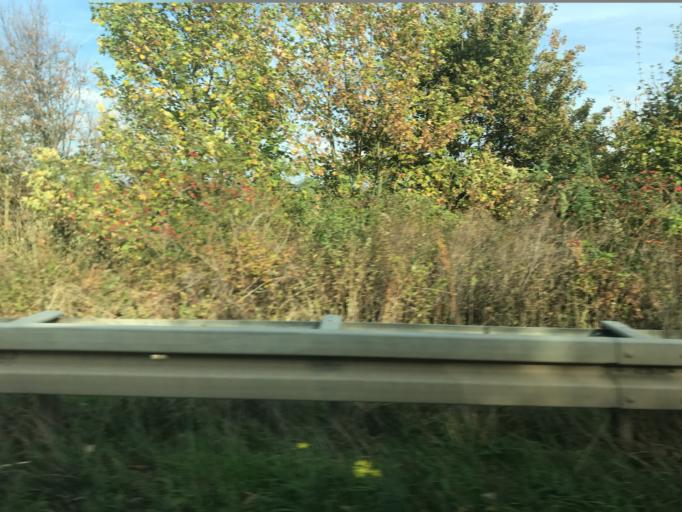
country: DE
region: North Rhine-Westphalia
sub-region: Regierungsbezirk Koln
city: Bergheim
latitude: 50.9196
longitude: 6.6146
